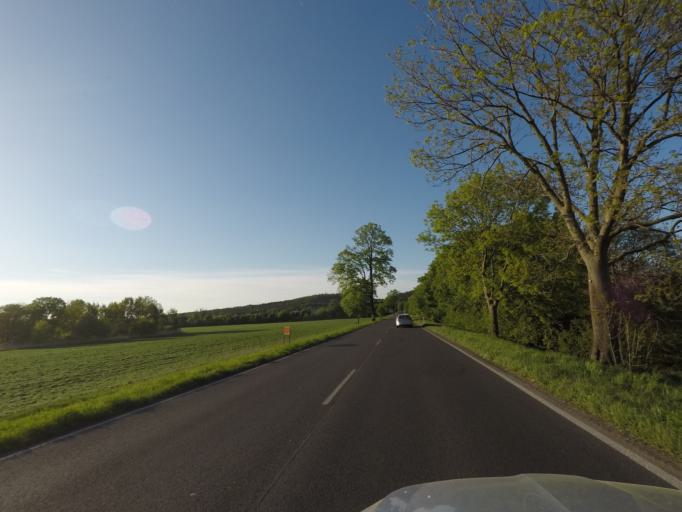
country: DE
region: Brandenburg
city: Bad Freienwalde
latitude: 52.8001
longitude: 14.0461
